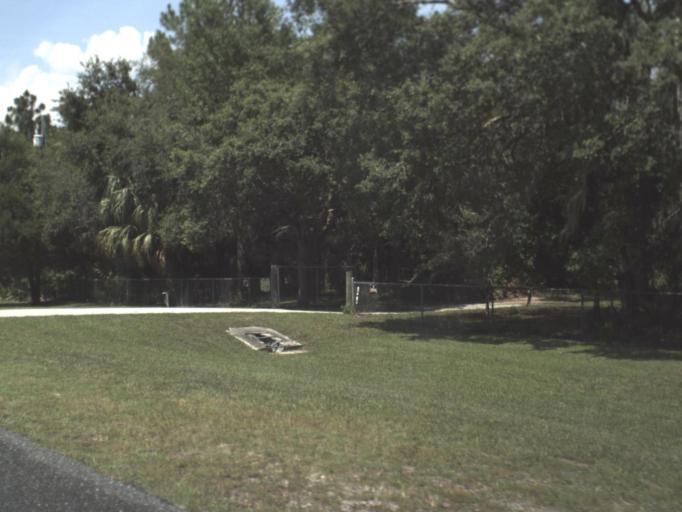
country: US
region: Florida
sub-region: Levy County
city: Inglis
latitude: 29.1321
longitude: -82.6369
